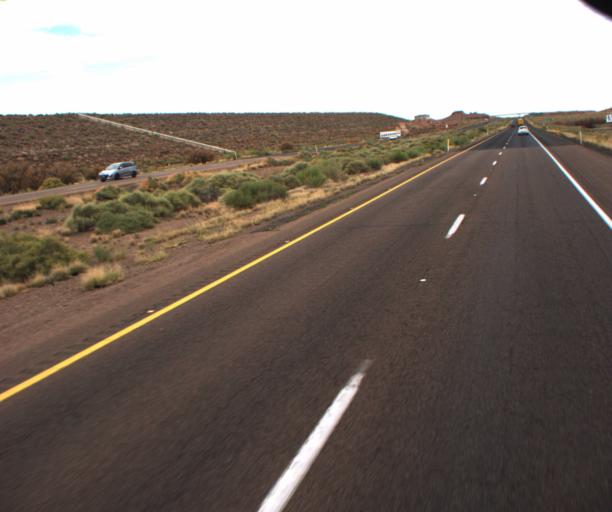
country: US
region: Arizona
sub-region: Navajo County
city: Joseph City
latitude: 34.9301
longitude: -110.2713
